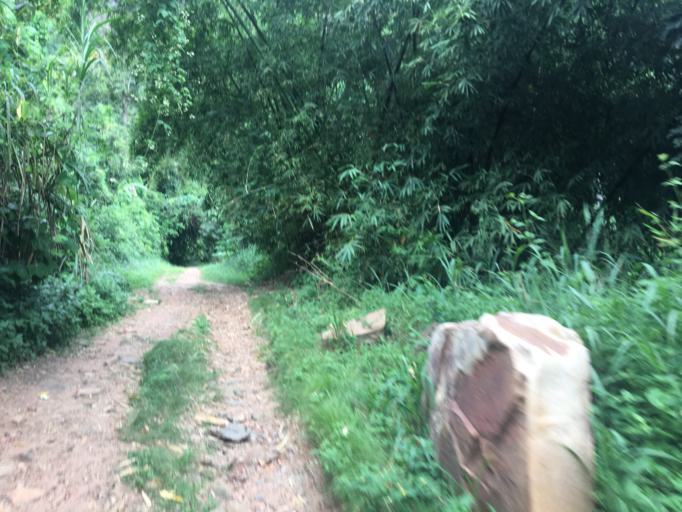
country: TG
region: Plateaux
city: Kpalime
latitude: 7.0070
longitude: 0.6462
